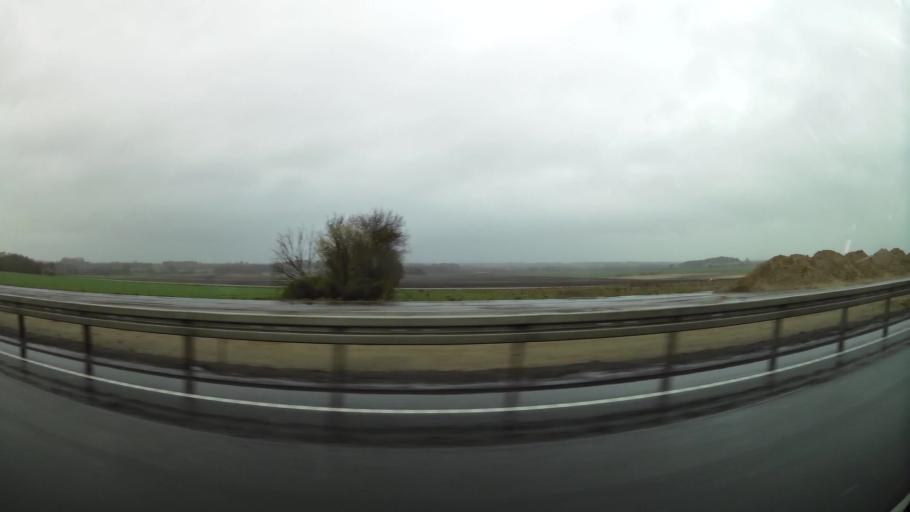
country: DK
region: Central Jutland
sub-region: Herning Kommune
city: Avlum
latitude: 56.2282
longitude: 8.8212
